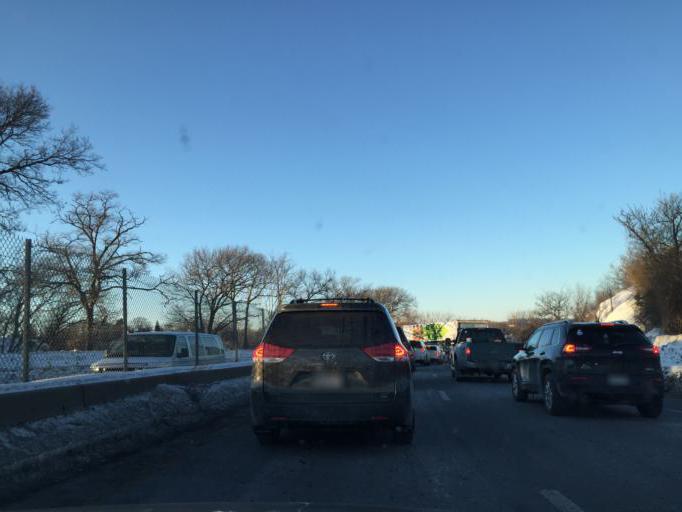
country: US
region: Massachusetts
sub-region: Essex County
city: Saugus
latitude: 42.4402
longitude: -71.0282
